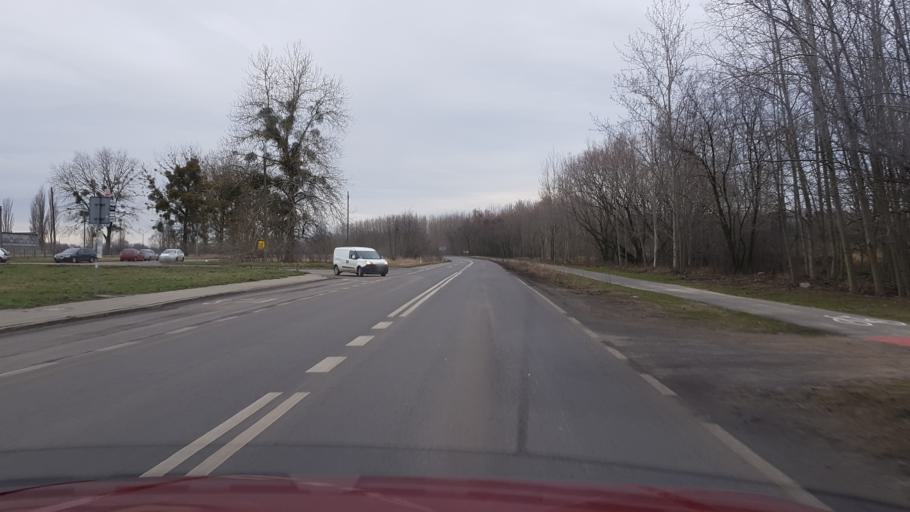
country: PL
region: West Pomeranian Voivodeship
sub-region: Powiat policki
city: Police
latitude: 53.5834
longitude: 14.5522
